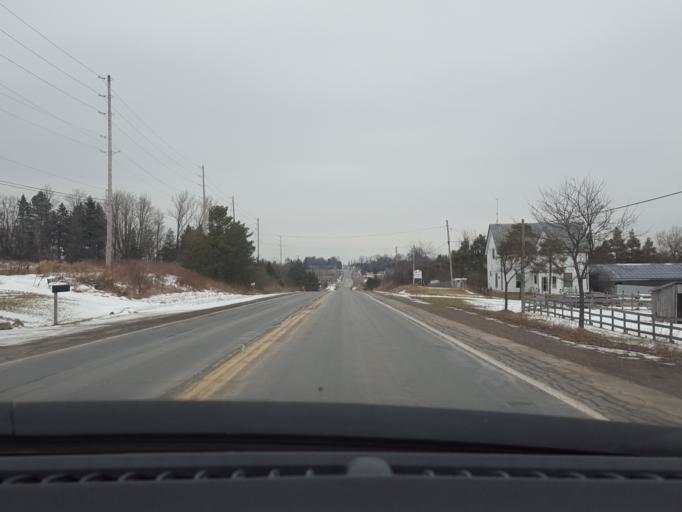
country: CA
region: Ontario
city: Newmarket
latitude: 44.0415
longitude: -79.4010
